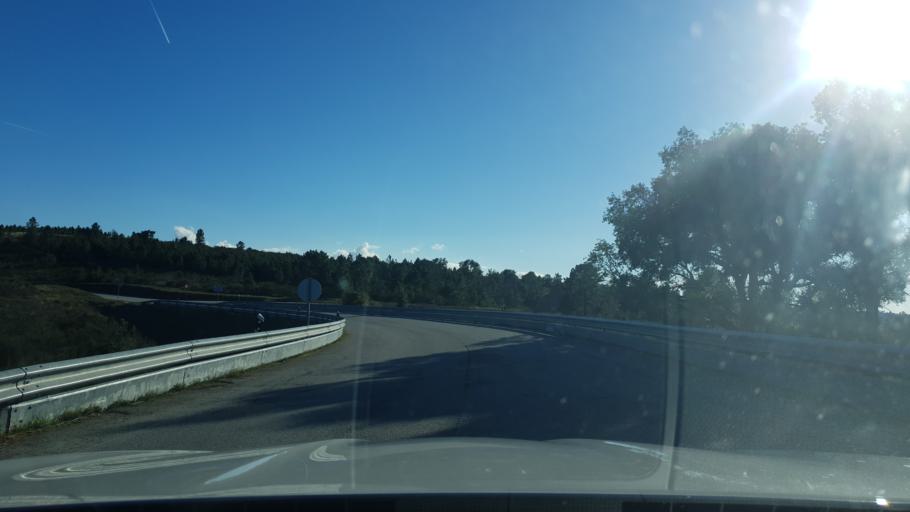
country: PT
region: Braganca
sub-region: Freixo de Espada A Cinta
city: Freixo de Espada a Cinta
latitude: 41.1204
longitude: -6.8212
